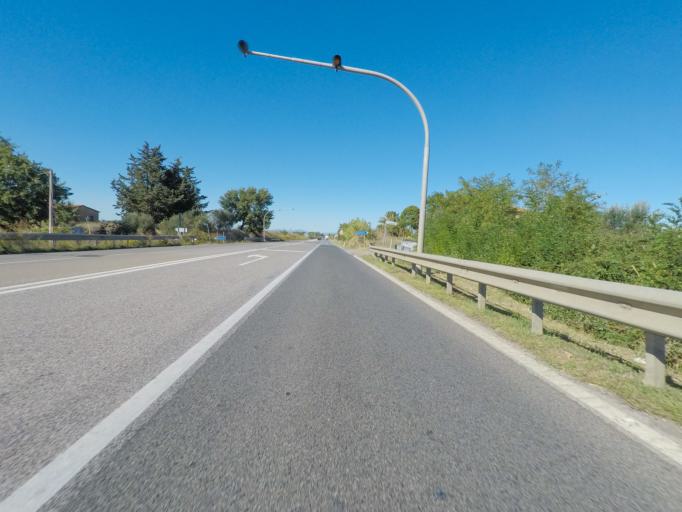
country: IT
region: Tuscany
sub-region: Provincia di Grosseto
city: Grosseto
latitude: 42.6779
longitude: 11.1407
